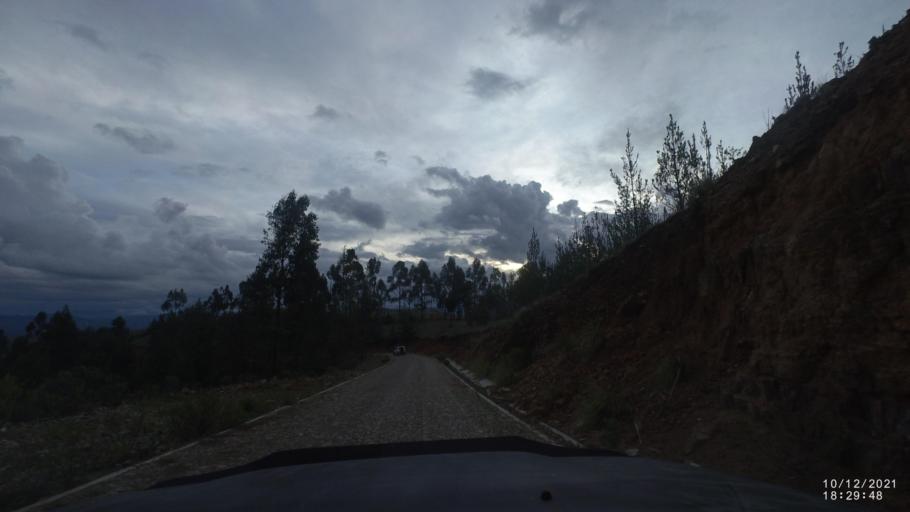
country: BO
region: Cochabamba
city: Tarata
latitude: -17.8117
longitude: -65.9796
